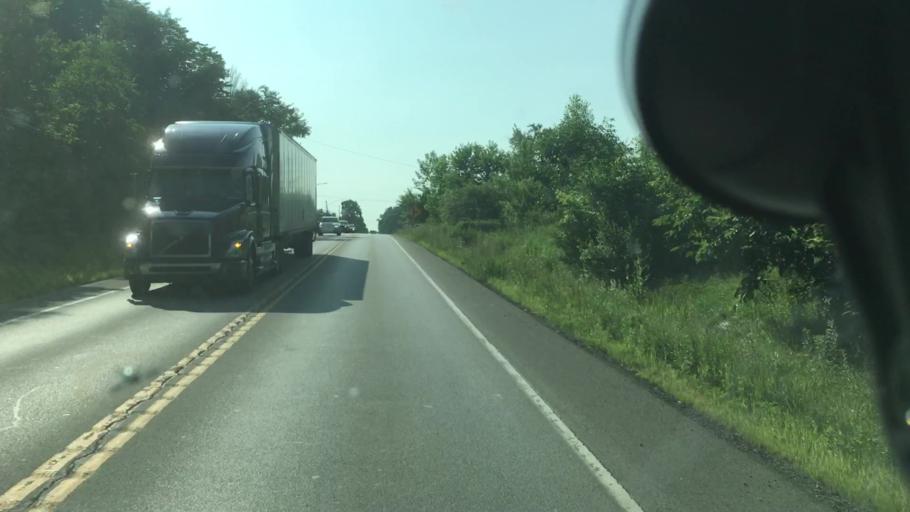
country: US
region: Pennsylvania
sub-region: Lawrence County
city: Bessemer
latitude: 41.0135
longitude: -80.4880
